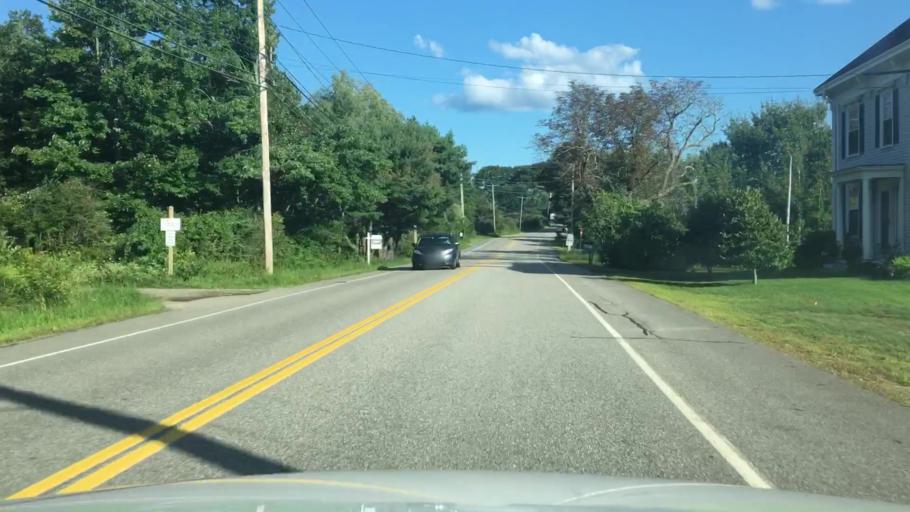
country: US
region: Maine
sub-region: Cumberland County
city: Scarborough
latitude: 43.5606
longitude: -70.3067
